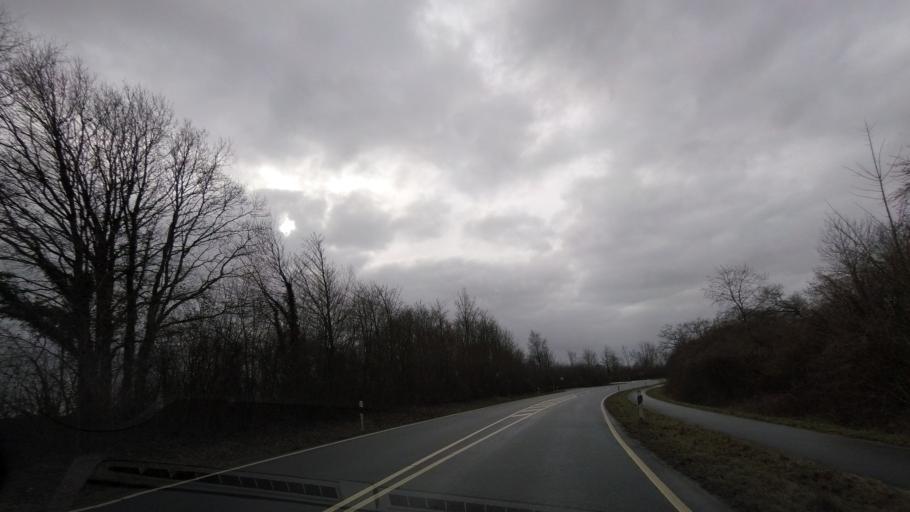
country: DE
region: Schleswig-Holstein
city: Schaalby
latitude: 54.5573
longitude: 9.6265
